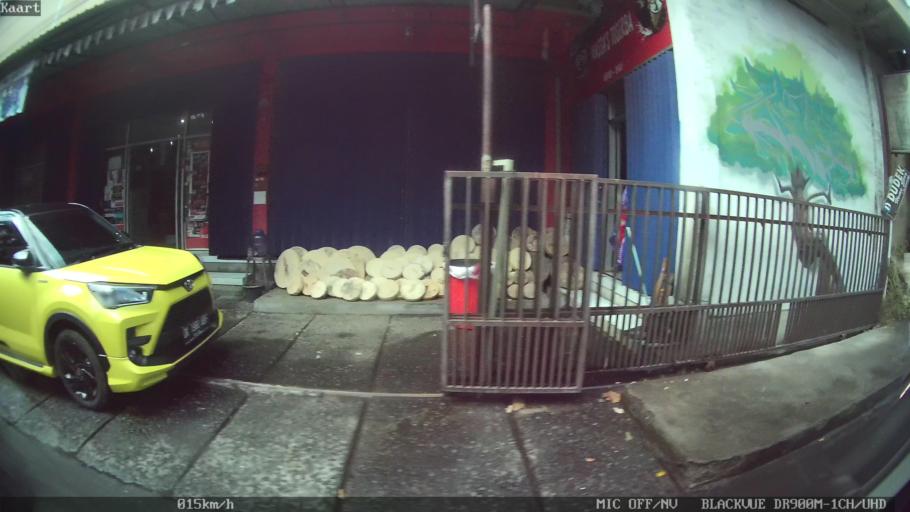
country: ID
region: Bali
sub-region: Kabupaten Gianyar
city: Ubud
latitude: -8.5239
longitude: 115.2698
